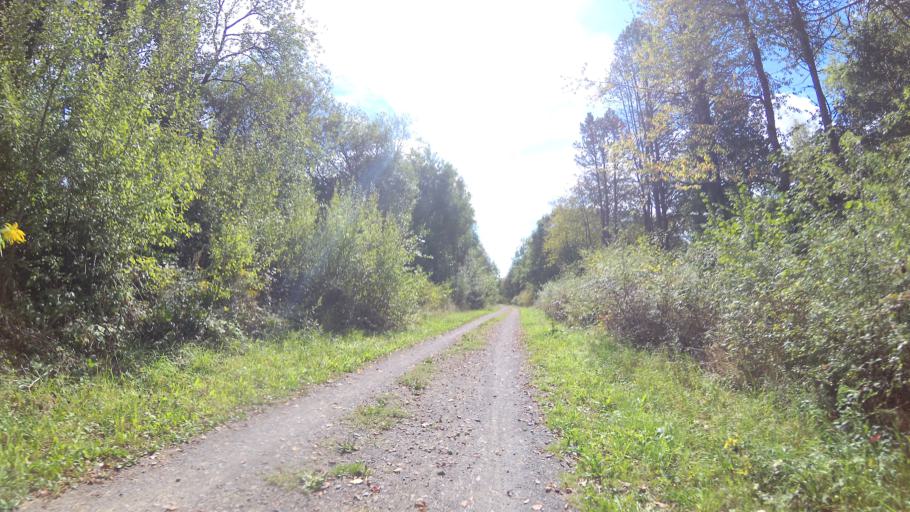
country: DE
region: Saarland
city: Freisen
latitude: 49.5216
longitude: 7.2351
